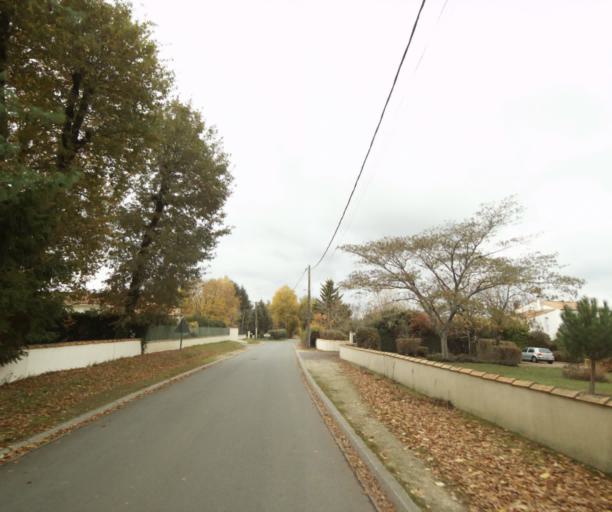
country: FR
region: Poitou-Charentes
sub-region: Departement de la Charente-Maritime
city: Saint-Georges-des-Coteaux
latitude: 45.7805
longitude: -0.6985
